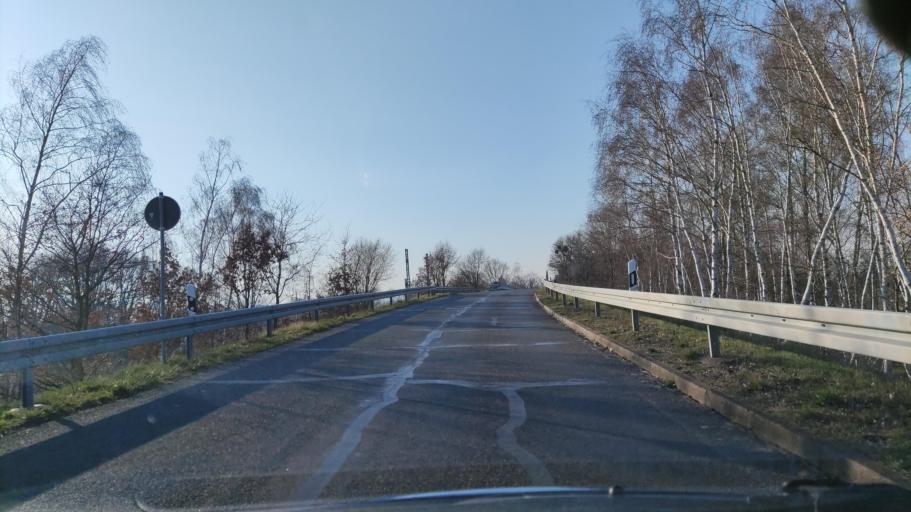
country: DE
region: Brandenburg
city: Wittenberge
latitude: 52.9675
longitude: 11.7436
